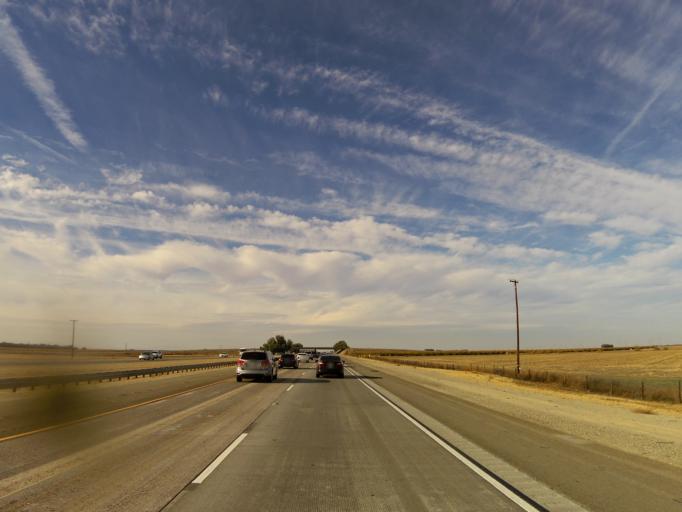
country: US
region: California
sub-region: Kern County
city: Lost Hills
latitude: 35.5717
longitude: -119.6125
